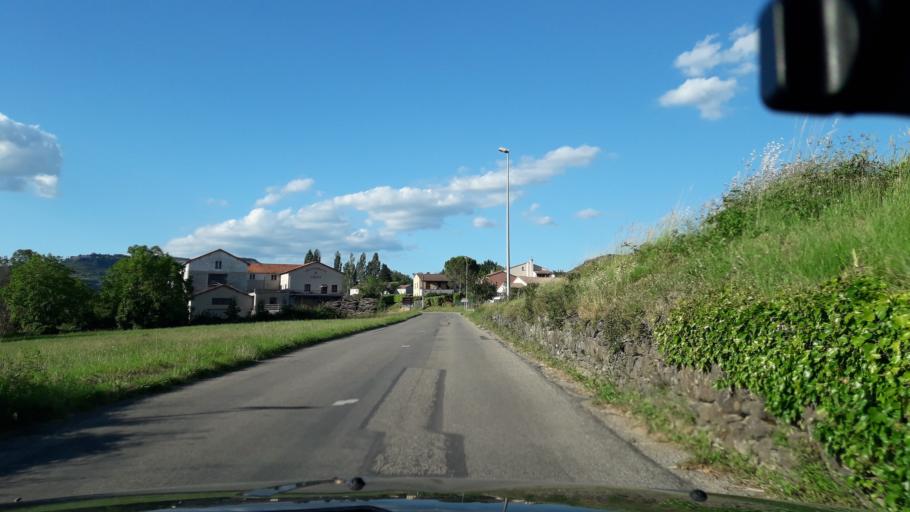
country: FR
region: Rhone-Alpes
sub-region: Departement de l'Ardeche
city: Lavilledieu
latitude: 44.6077
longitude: 4.4718
